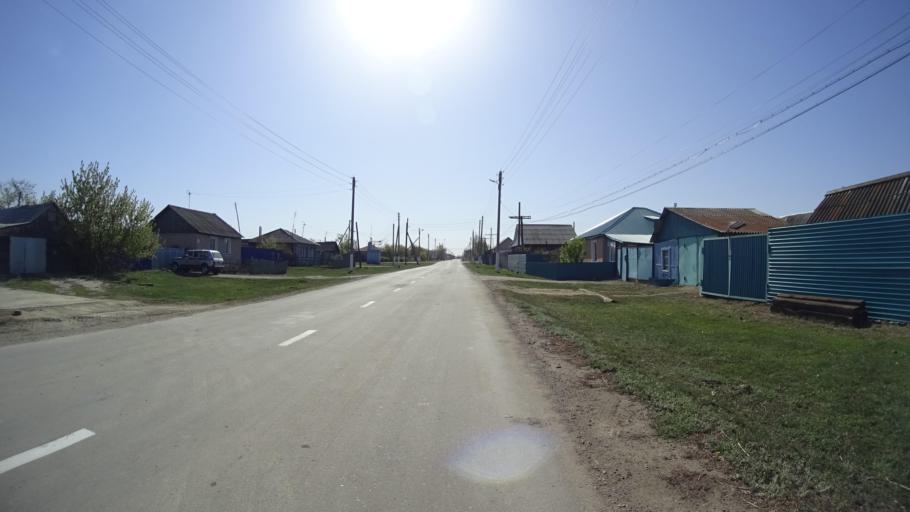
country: RU
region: Chelyabinsk
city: Chesma
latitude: 53.7994
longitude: 61.0243
